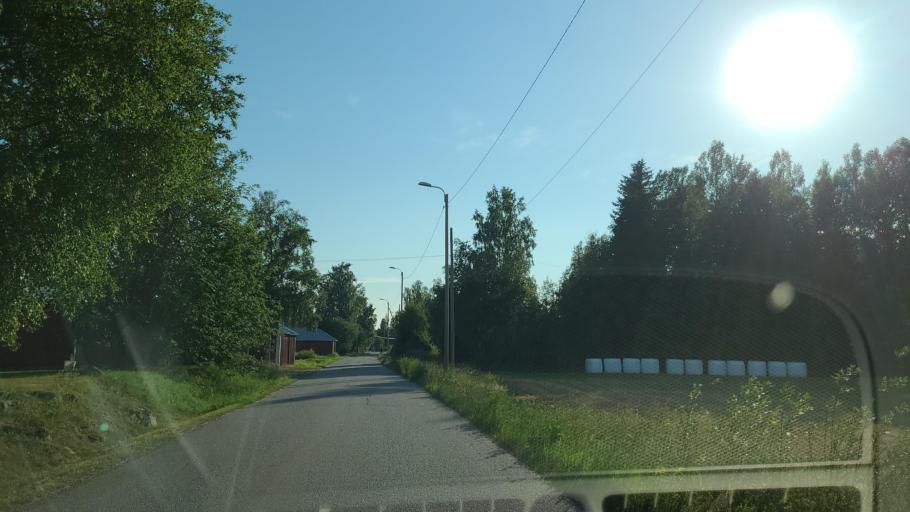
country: FI
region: Ostrobothnia
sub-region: Vaasa
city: Replot
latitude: 63.3463
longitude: 21.3238
